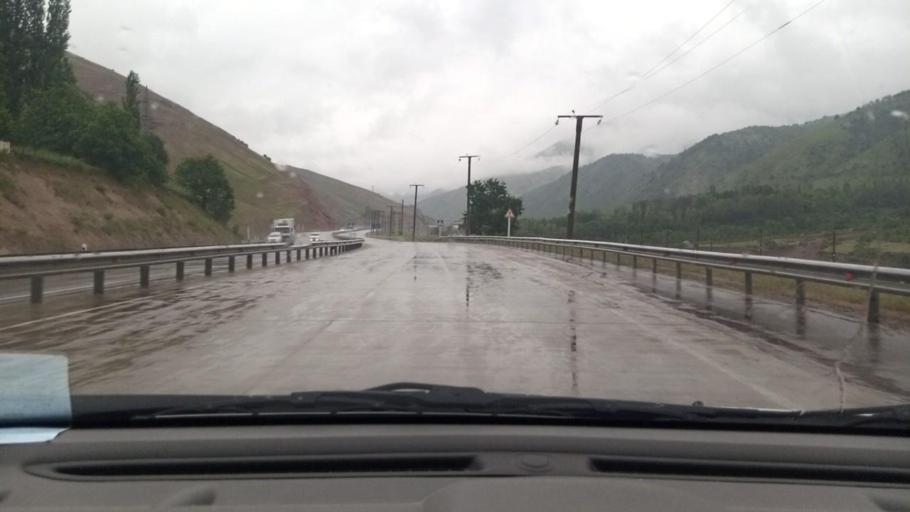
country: UZ
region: Toshkent
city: Angren
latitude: 41.1462
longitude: 70.4110
